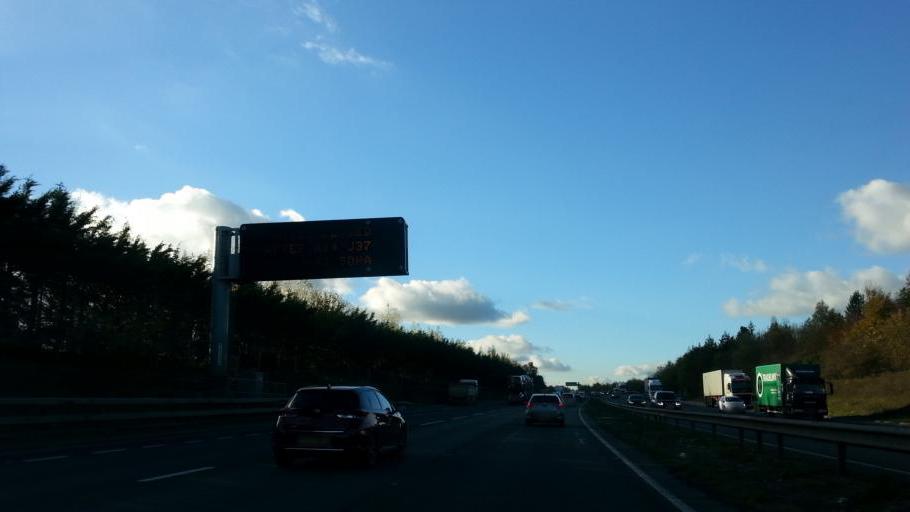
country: GB
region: England
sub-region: Suffolk
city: Newmarket
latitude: 52.2675
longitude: 0.4201
